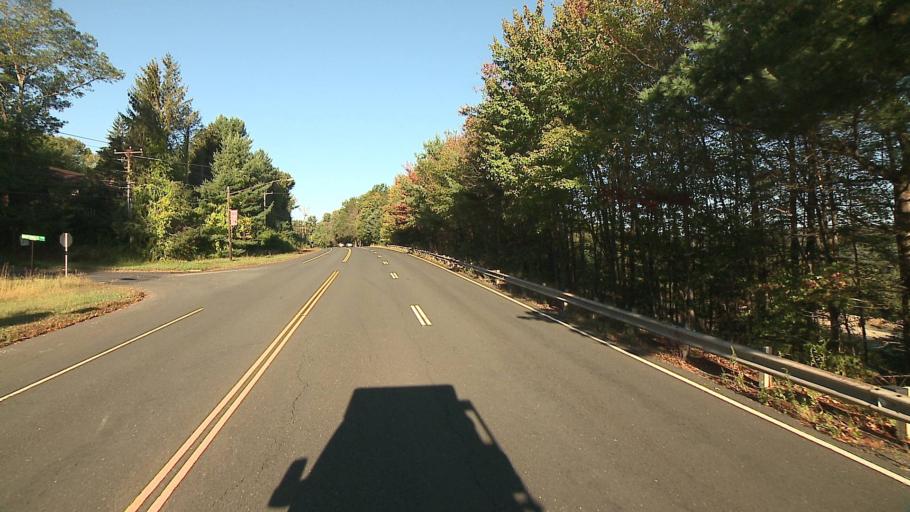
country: US
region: Connecticut
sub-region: Litchfield County
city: New Hartford Center
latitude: 41.8311
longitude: -73.0205
